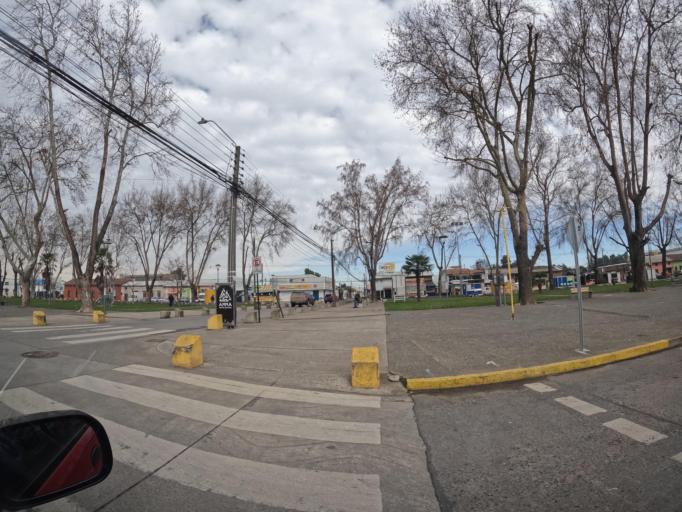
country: CL
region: Maule
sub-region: Provincia de Linares
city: Linares
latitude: -35.8489
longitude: -71.5968
